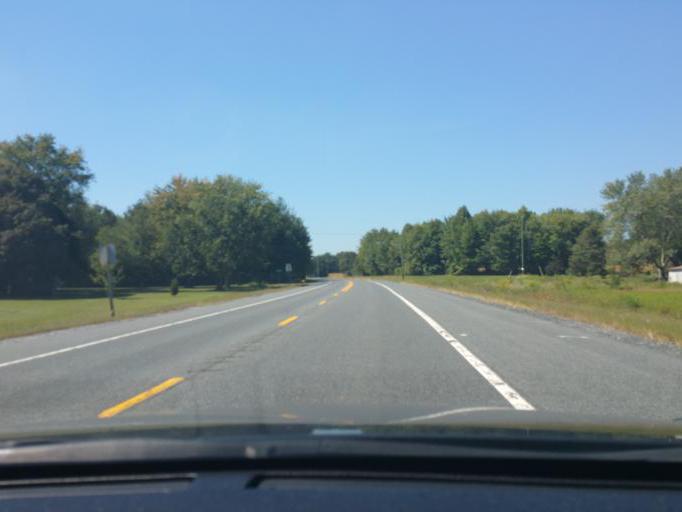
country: US
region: Maryland
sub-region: Harford County
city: Aberdeen
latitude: 39.5785
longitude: -76.1968
